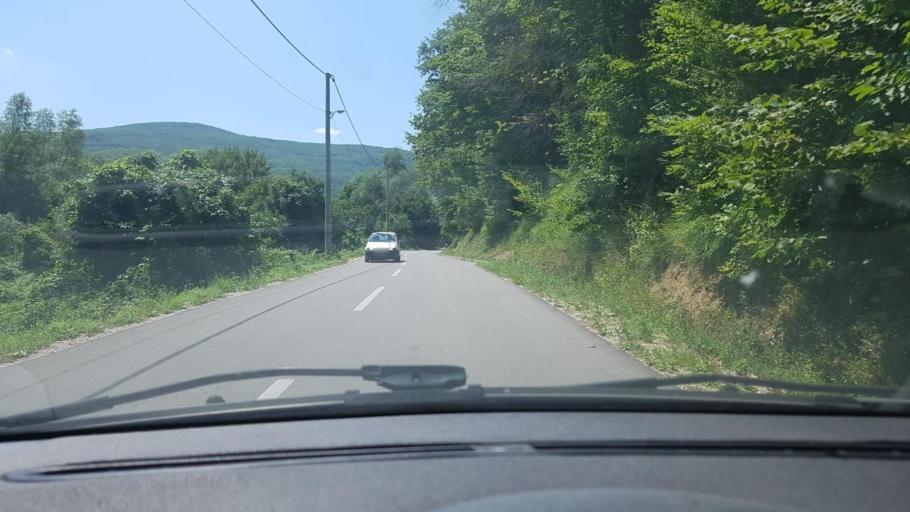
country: BA
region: Federation of Bosnia and Herzegovina
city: Orasac
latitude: 44.5679
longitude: 16.0938
